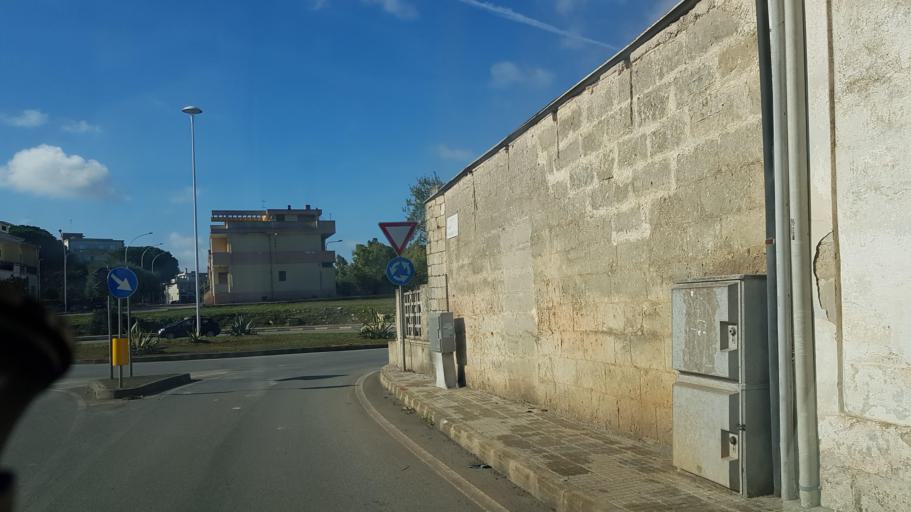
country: IT
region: Apulia
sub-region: Provincia di Brindisi
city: San Vito dei Normanni
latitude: 40.6627
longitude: 17.7059
